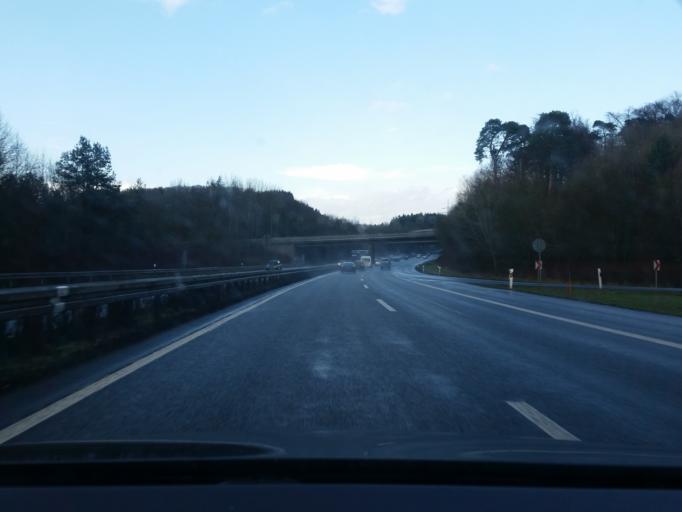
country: DE
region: Hesse
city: Lollar
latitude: 50.6288
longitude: 8.7145
